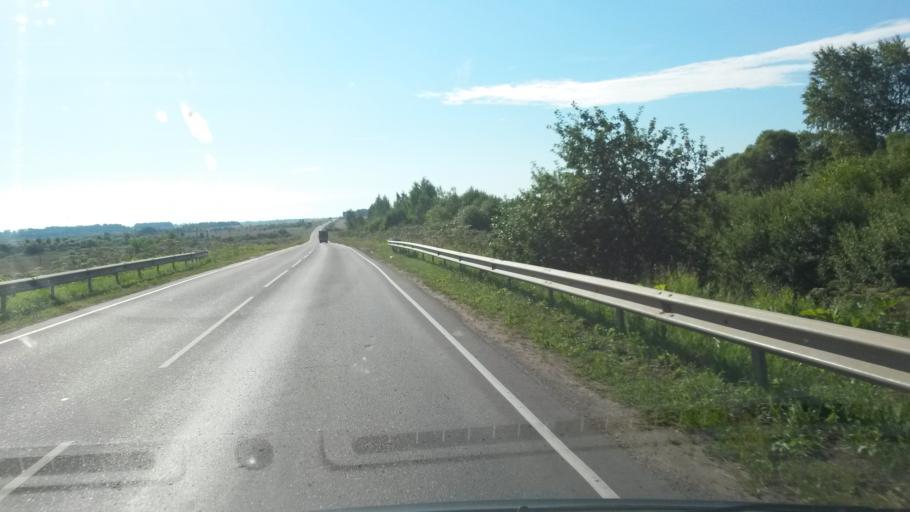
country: RU
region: Jaroslavl
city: Dubki
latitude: 57.1995
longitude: 40.3371
